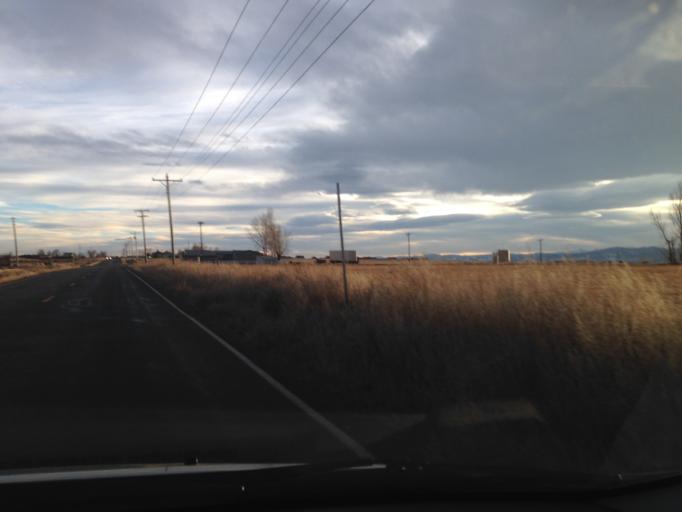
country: US
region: Colorado
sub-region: Weld County
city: Frederick
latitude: 40.1039
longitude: -104.9989
